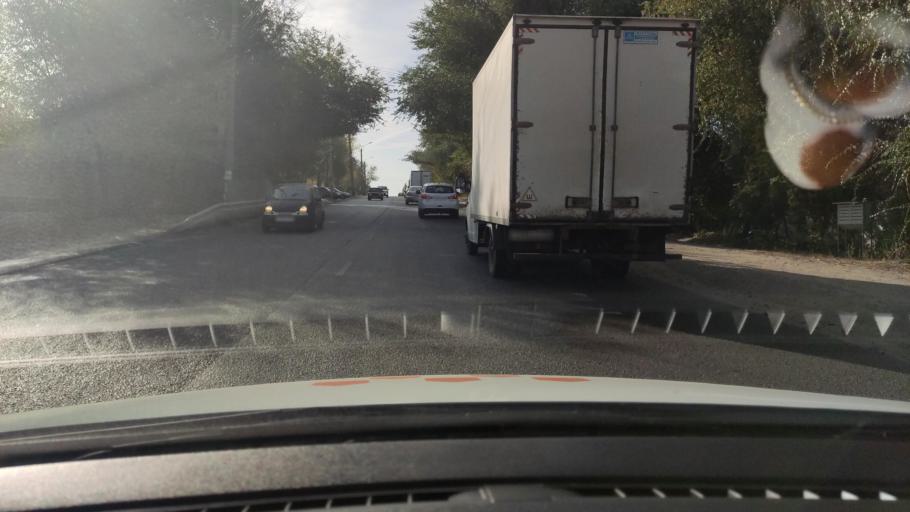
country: RU
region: Voronezj
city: Voronezh
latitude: 51.6923
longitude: 39.1647
